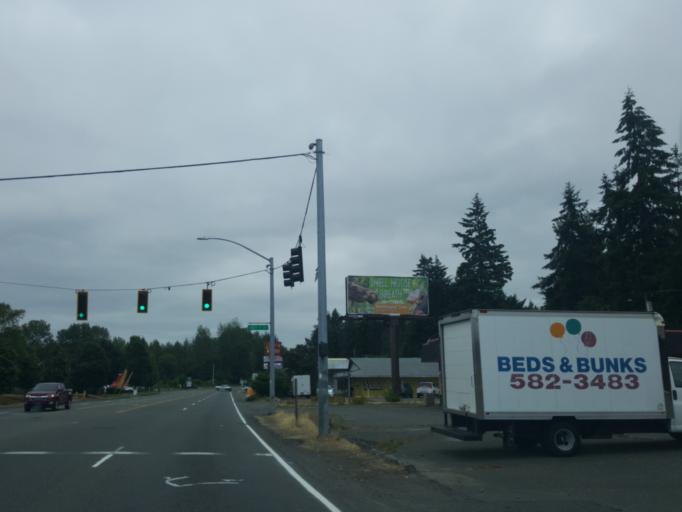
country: US
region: Washington
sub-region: Pierce County
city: Lakewood
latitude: 47.1671
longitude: -122.4915
